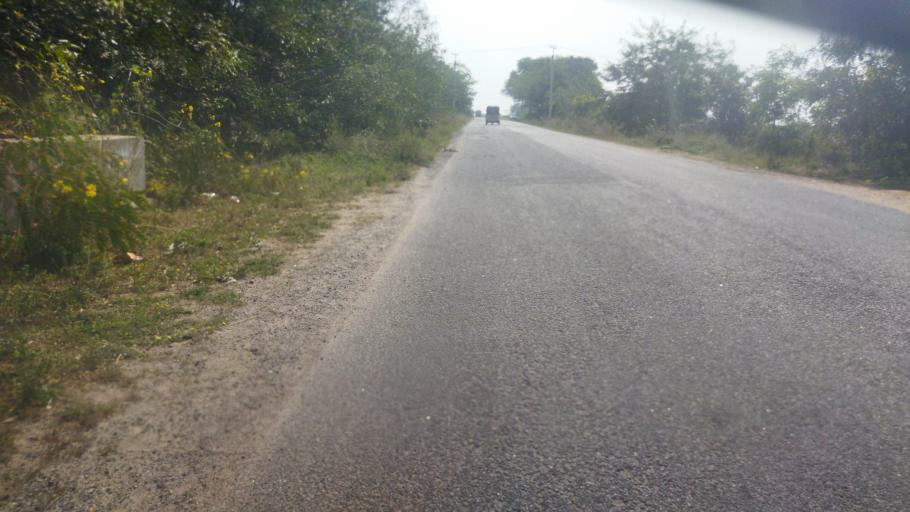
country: IN
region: Telangana
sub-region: Nalgonda
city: Nalgonda
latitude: 17.1036
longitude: 79.2823
